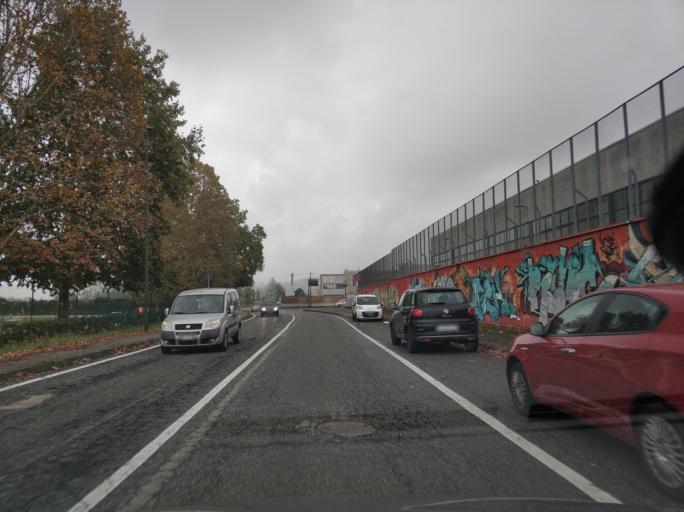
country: IT
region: Piedmont
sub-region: Provincia di Torino
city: Settimo Torinese
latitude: 45.1252
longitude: 7.7523
